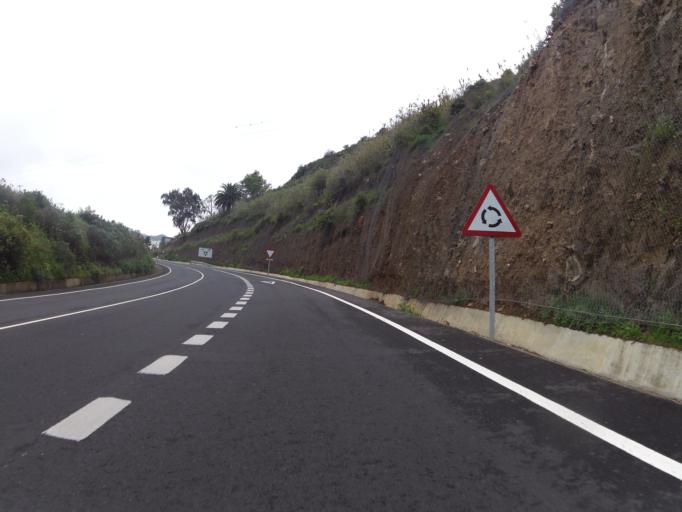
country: ES
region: Canary Islands
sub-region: Provincia de Las Palmas
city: Teror
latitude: 28.0694
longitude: -15.5372
